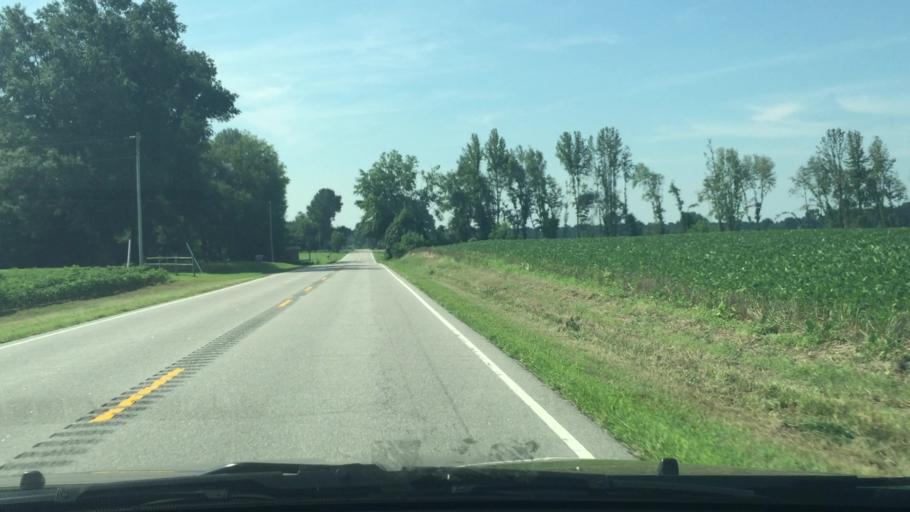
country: US
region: Virginia
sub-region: Southampton County
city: Courtland
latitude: 36.7991
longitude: -77.1288
